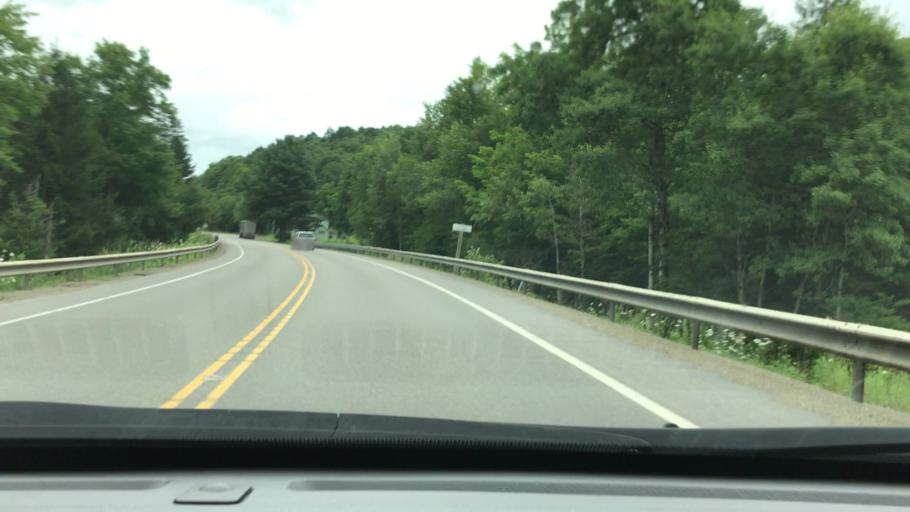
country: US
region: Pennsylvania
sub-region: McKean County
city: Kane
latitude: 41.6708
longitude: -78.6804
